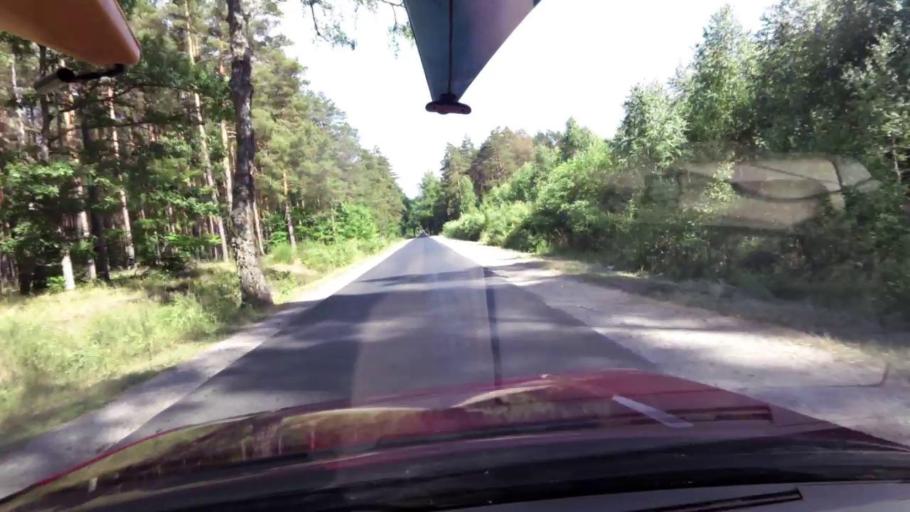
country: PL
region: Pomeranian Voivodeship
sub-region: Powiat bytowski
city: Miastko
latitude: 54.1099
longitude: 16.9637
